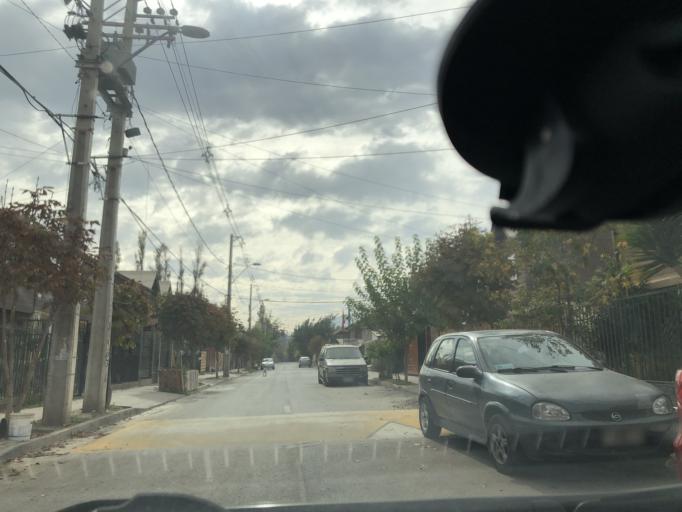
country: CL
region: Santiago Metropolitan
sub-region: Provincia de Cordillera
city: Puente Alto
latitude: -33.6114
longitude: -70.5273
